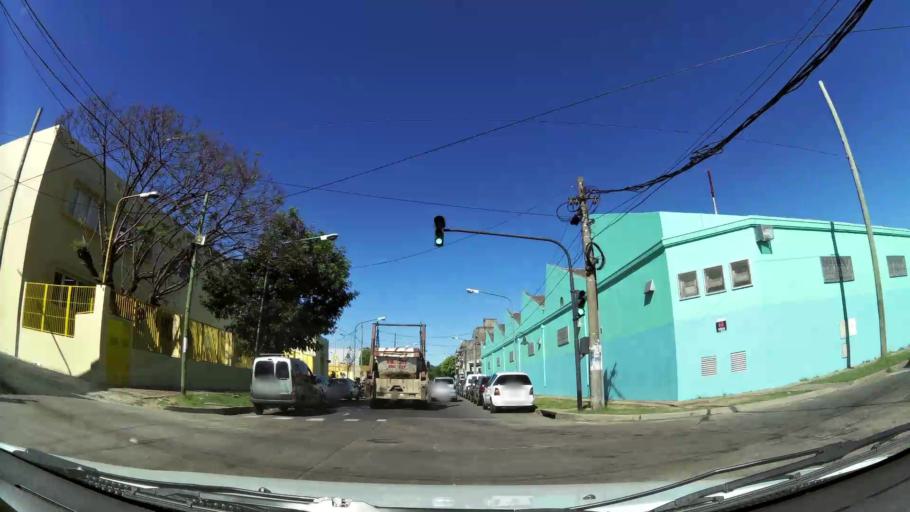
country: AR
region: Buenos Aires
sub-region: Partido de General San Martin
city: General San Martin
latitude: -34.5433
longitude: -58.5168
